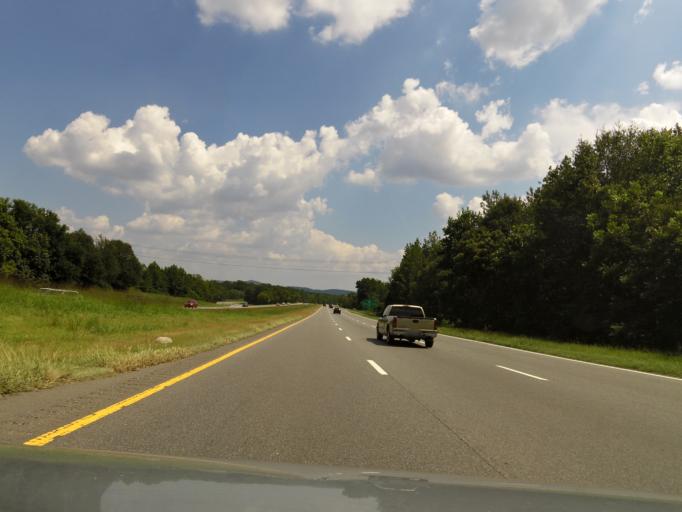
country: US
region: North Carolina
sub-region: Cleveland County
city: Kings Mountain
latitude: 35.2495
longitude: -81.3355
